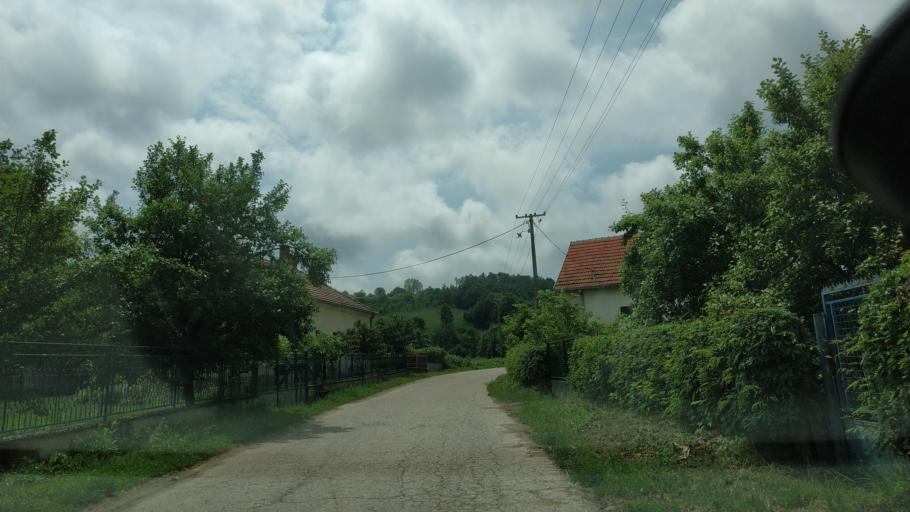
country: RS
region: Central Serbia
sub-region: Nisavski Okrug
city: Aleksinac
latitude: 43.4263
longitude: 21.7095
